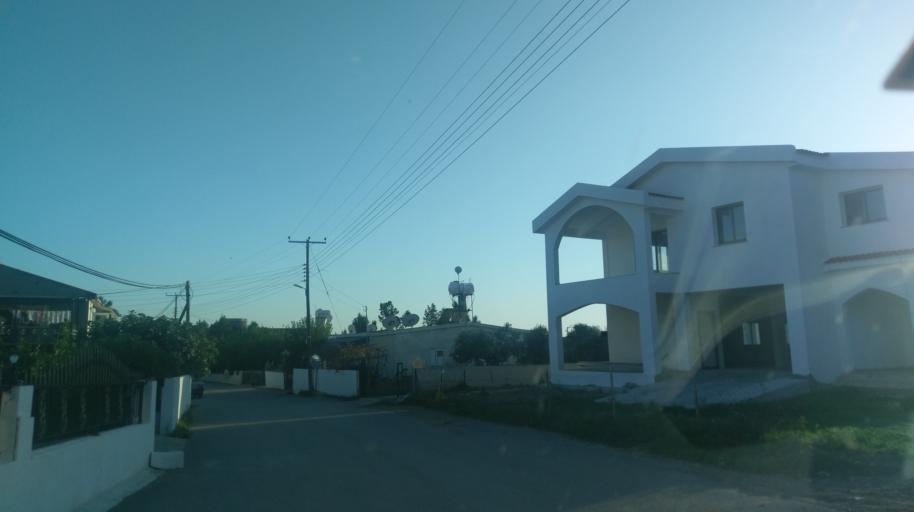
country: CY
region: Ammochostos
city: Lefkonoiko
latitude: 35.2576
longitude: 33.5488
